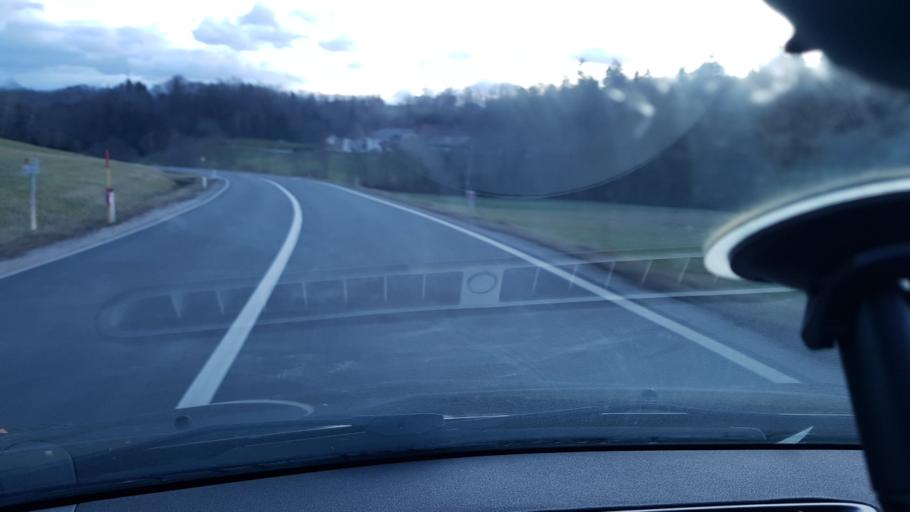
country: SI
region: Rogaska Slatina
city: Rogaska Slatina
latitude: 46.2501
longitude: 15.6049
